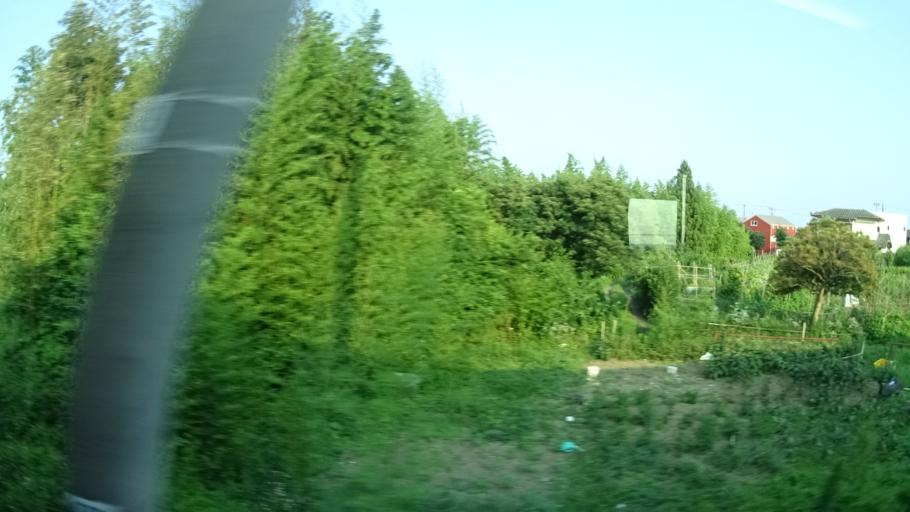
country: JP
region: Ibaraki
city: Hitachi
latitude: 36.5741
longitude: 140.6511
